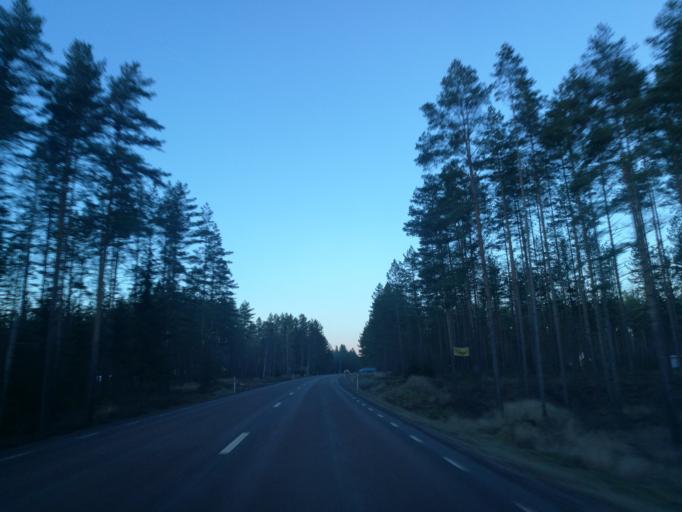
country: SE
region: Vaermland
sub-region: Eda Kommun
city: Charlottenberg
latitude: 59.9079
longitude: 12.2753
